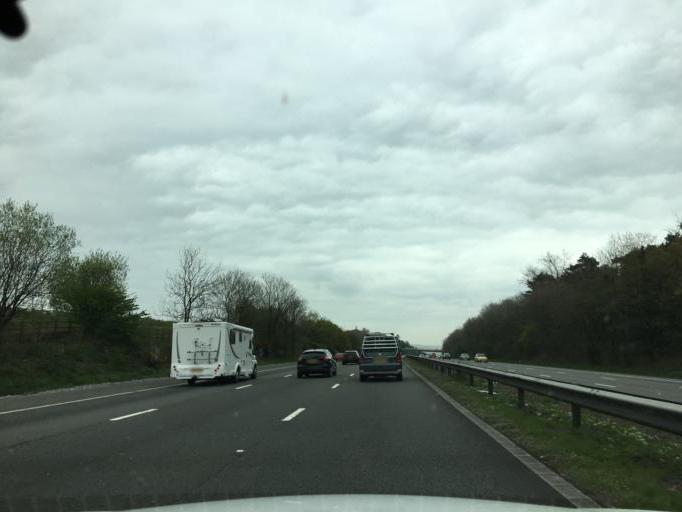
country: GB
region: Wales
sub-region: Bridgend county borough
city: Aberkenfig
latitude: 51.5303
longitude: -3.6193
